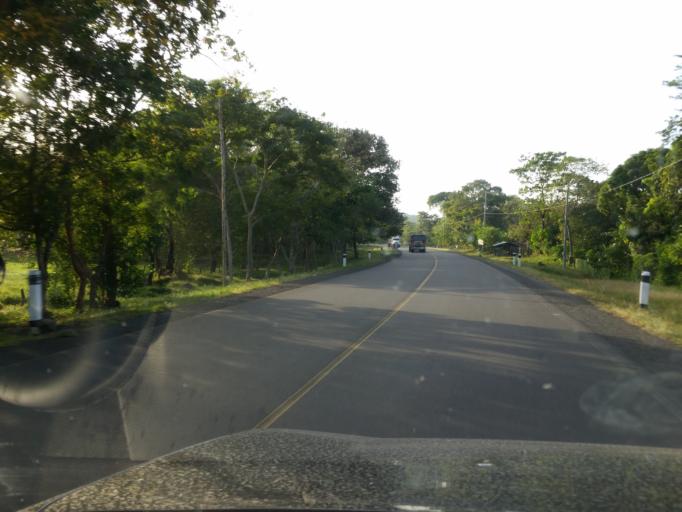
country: NI
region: Rio San Juan
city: San Miguelito
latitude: 11.3948
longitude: -84.8047
